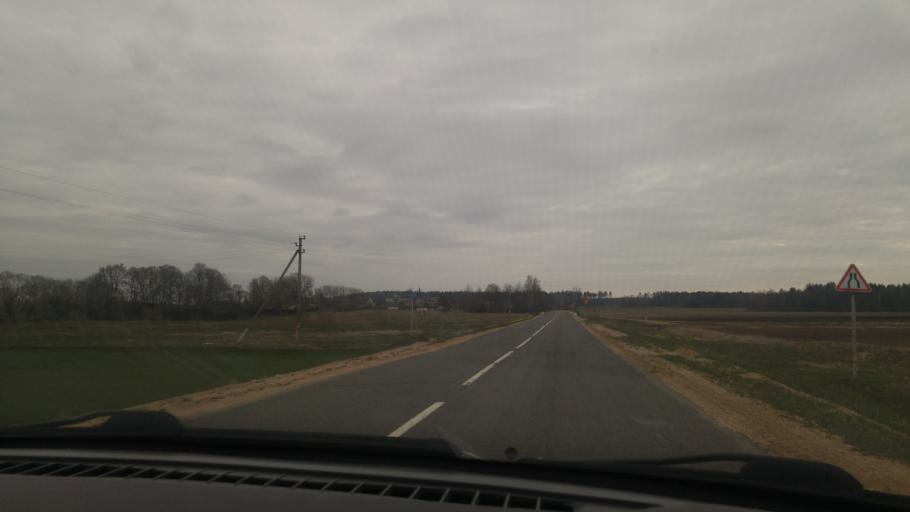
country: BY
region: Minsk
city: Chervyen'
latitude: 53.7277
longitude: 28.2723
